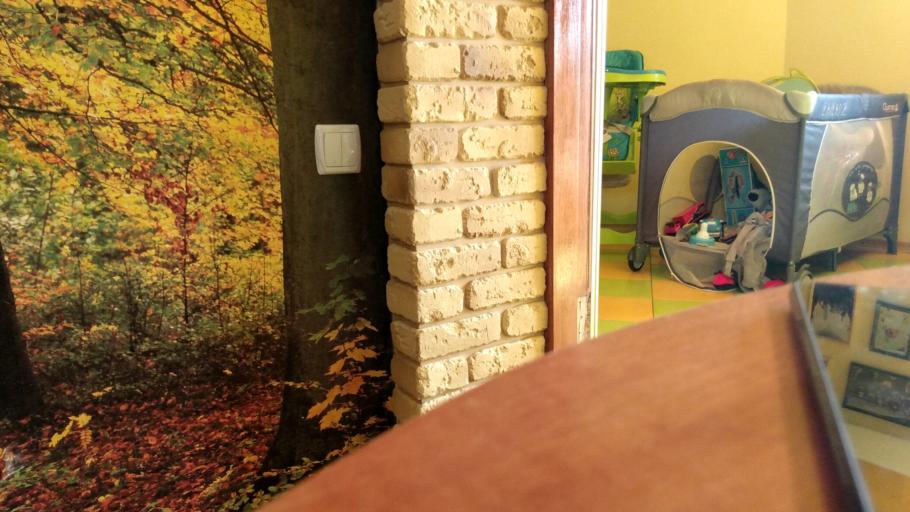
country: RU
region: Tverskaya
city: Sakharovo
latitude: 56.9147
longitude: 36.0332
